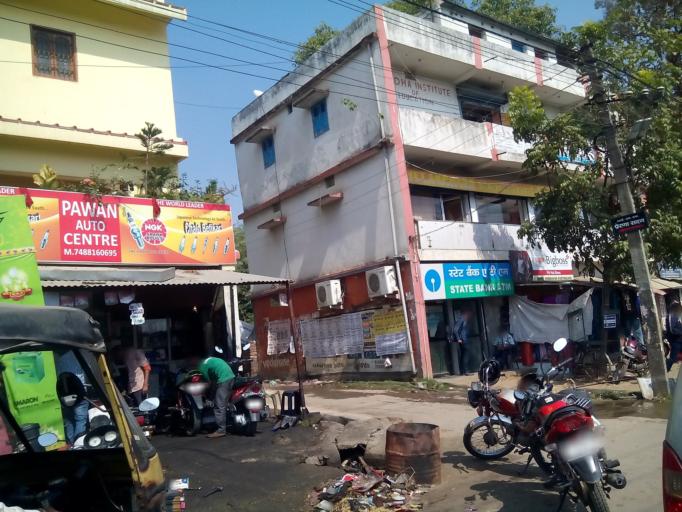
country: IN
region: Jharkhand
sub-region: Ranchi
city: Ranchi
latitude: 23.3766
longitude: 85.3554
